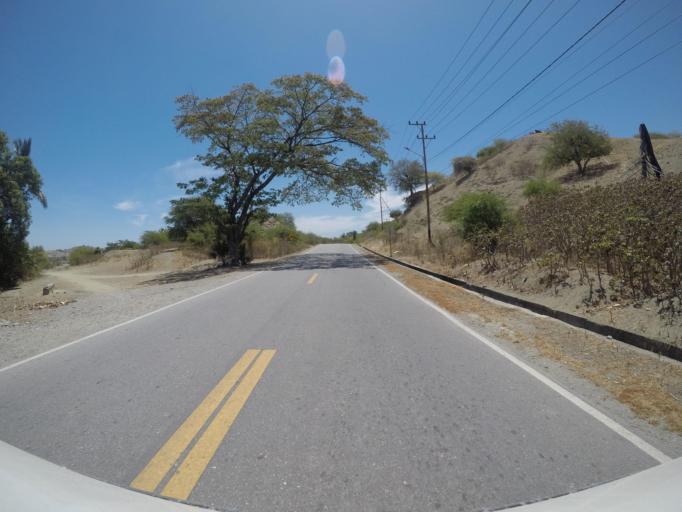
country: TL
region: Manatuto
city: Manatuto
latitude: -8.5266
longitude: 126.0047
